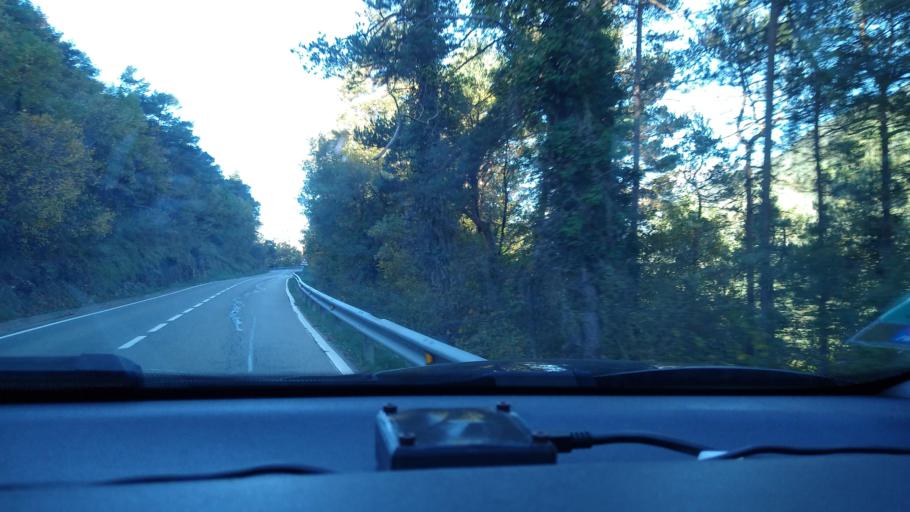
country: ES
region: Catalonia
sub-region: Provincia de Barcelona
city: Guardiola de Bergueda
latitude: 42.2211
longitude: 1.8514
